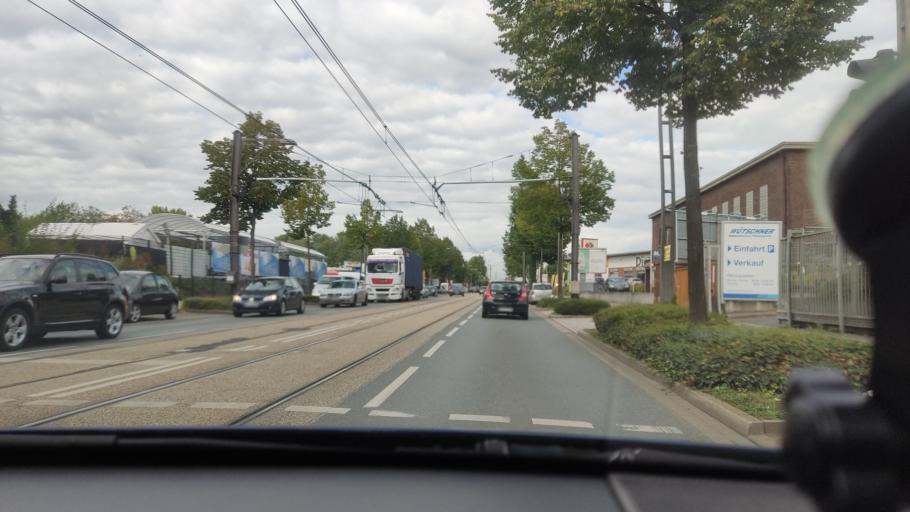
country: DE
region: North Rhine-Westphalia
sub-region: Regierungsbezirk Arnsberg
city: Dortmund
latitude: 51.5445
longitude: 7.4598
